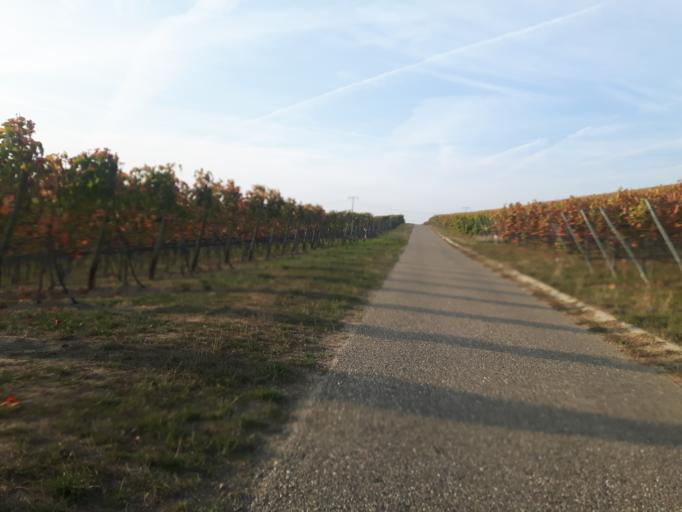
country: DE
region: Baden-Wuerttemberg
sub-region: Regierungsbezirk Stuttgart
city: Talheim
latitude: 49.0701
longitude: 9.1745
